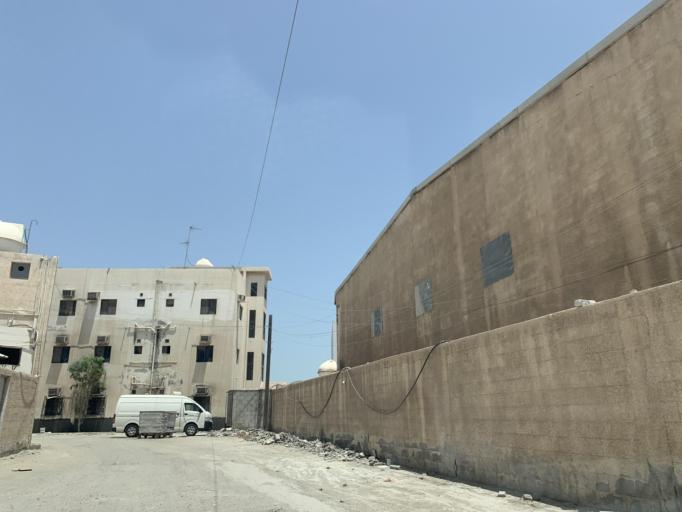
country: BH
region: Northern
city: Sitrah
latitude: 26.1746
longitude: 50.6089
